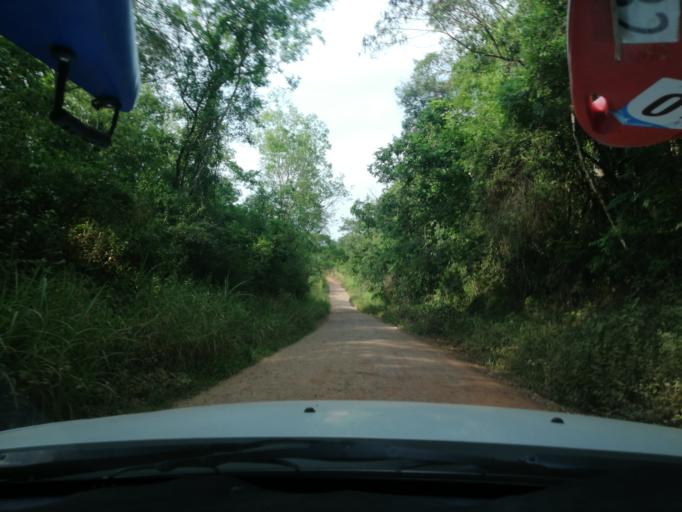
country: AR
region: Misiones
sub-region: Departamento de San Ignacio
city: San Ignacio
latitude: -27.2885
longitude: -55.5623
